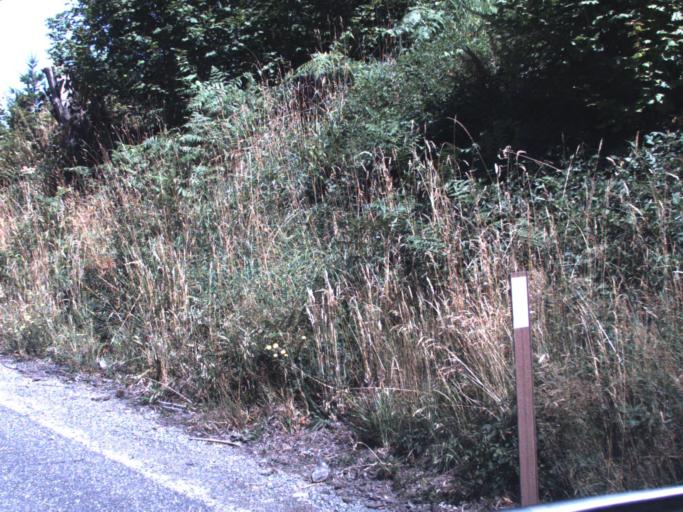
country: US
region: Washington
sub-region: King County
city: Enumclaw
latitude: 47.1570
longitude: -121.8648
